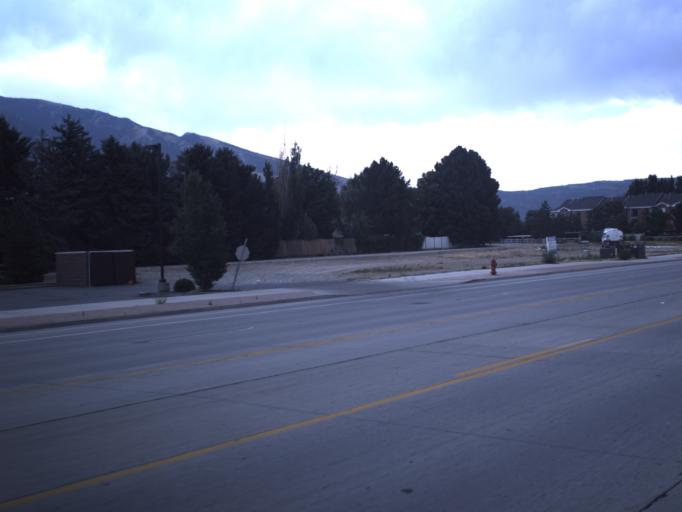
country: US
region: Utah
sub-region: Salt Lake County
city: White City
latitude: 40.5542
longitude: -111.8723
